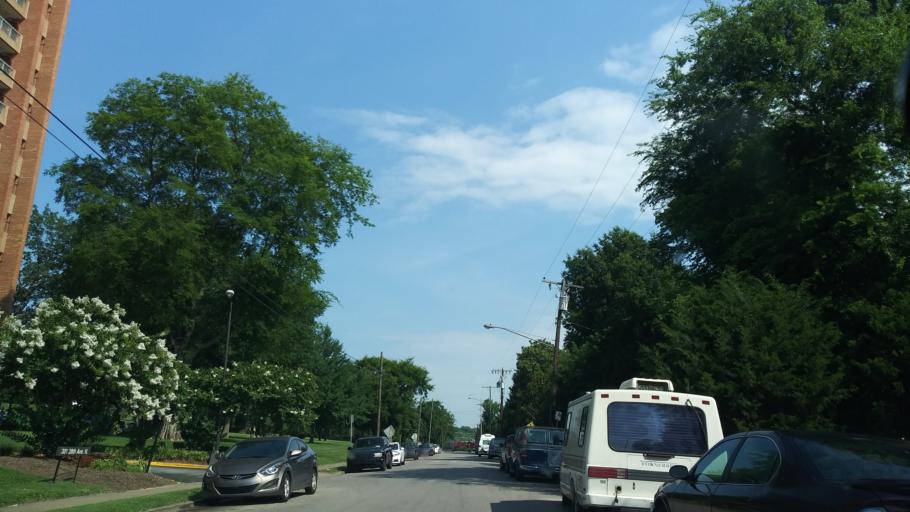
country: US
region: Tennessee
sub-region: Davidson County
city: Nashville
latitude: 36.1475
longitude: -86.8142
